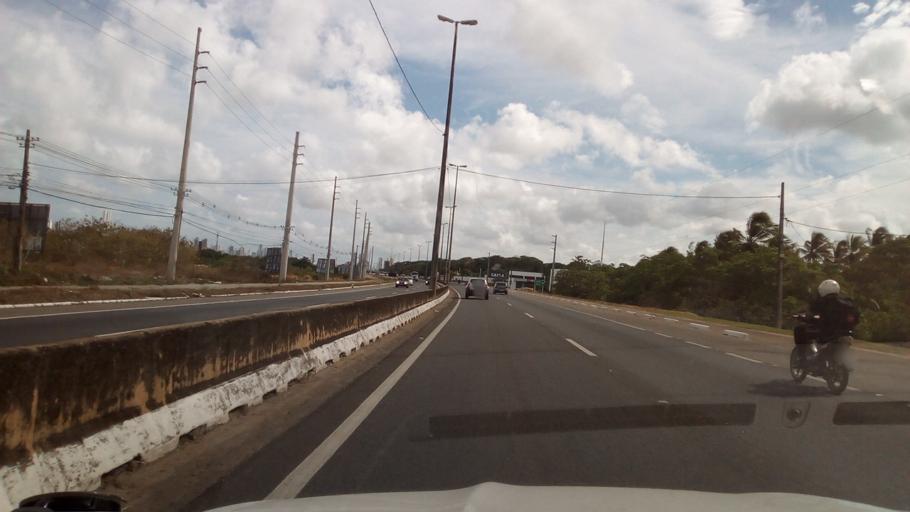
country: BR
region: Paraiba
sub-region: Joao Pessoa
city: Joao Pessoa
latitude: -7.0548
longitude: -34.8506
